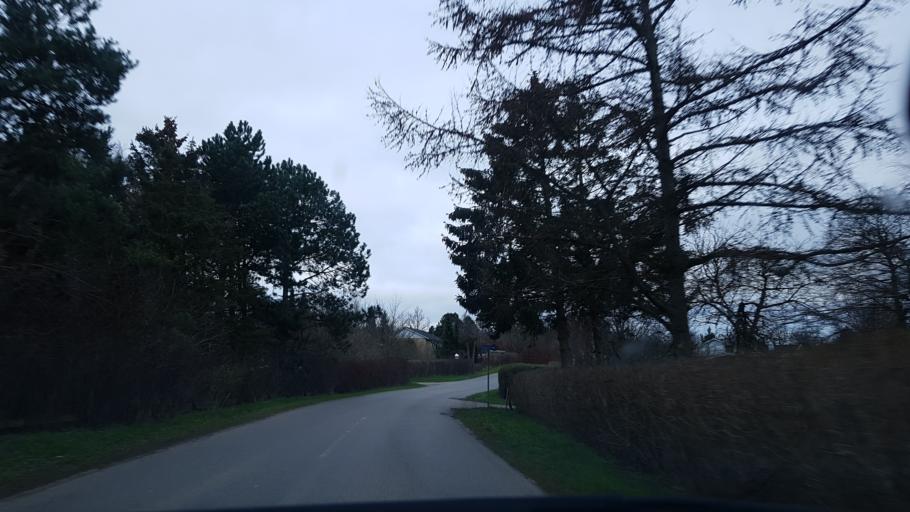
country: DK
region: Zealand
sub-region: Odsherred Kommune
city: Hojby
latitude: 55.9396
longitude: 11.6113
